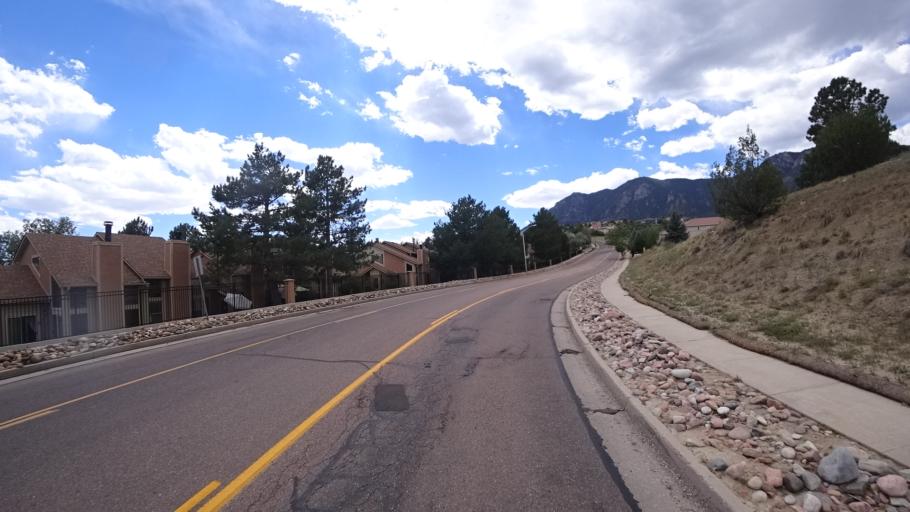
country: US
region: Colorado
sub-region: El Paso County
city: Stratmoor
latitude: 38.7736
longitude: -104.8218
